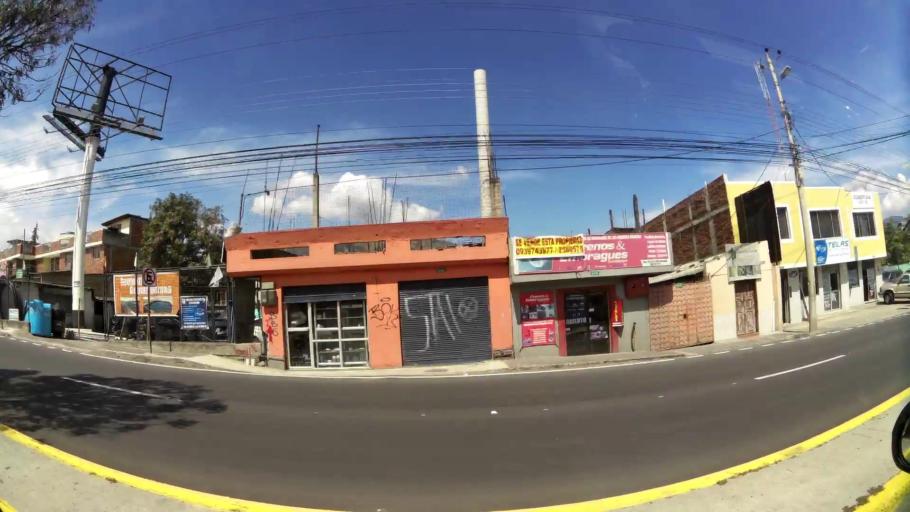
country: EC
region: Pichincha
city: Quito
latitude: -0.2169
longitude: -78.4019
